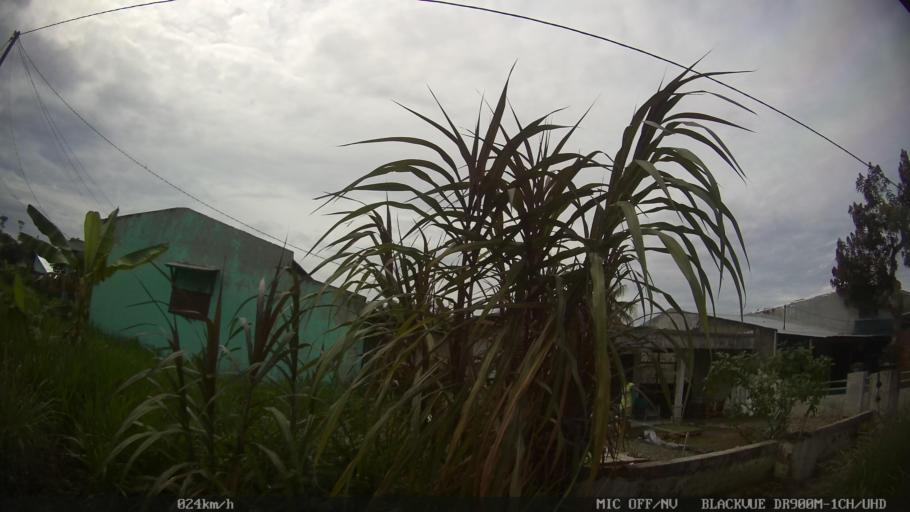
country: ID
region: North Sumatra
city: Sunggal
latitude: 3.5865
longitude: 98.5828
